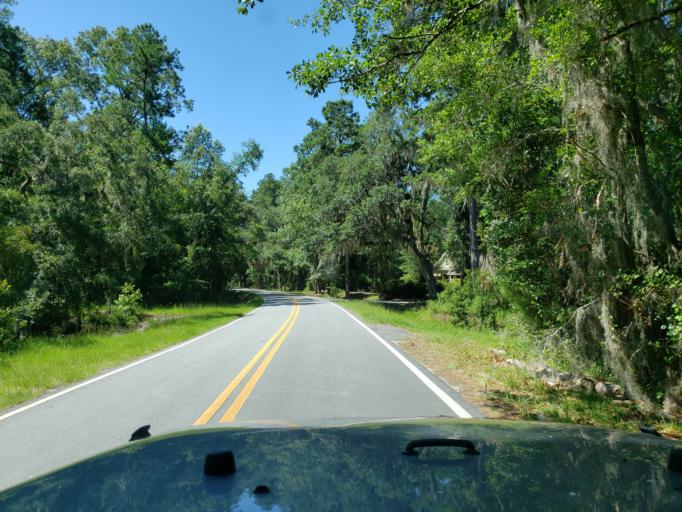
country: US
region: Georgia
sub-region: Chatham County
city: Georgetown
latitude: 31.9646
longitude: -81.2189
